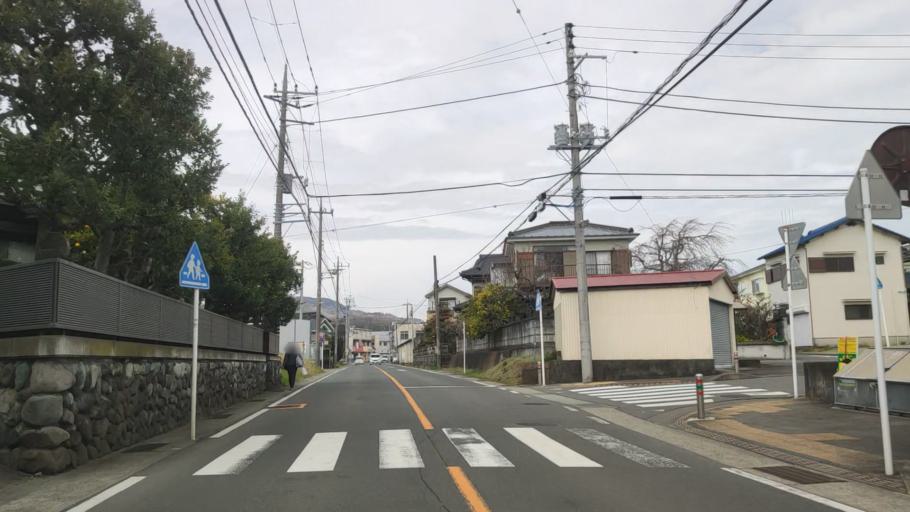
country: JP
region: Kanagawa
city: Ninomiya
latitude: 35.2990
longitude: 139.2300
